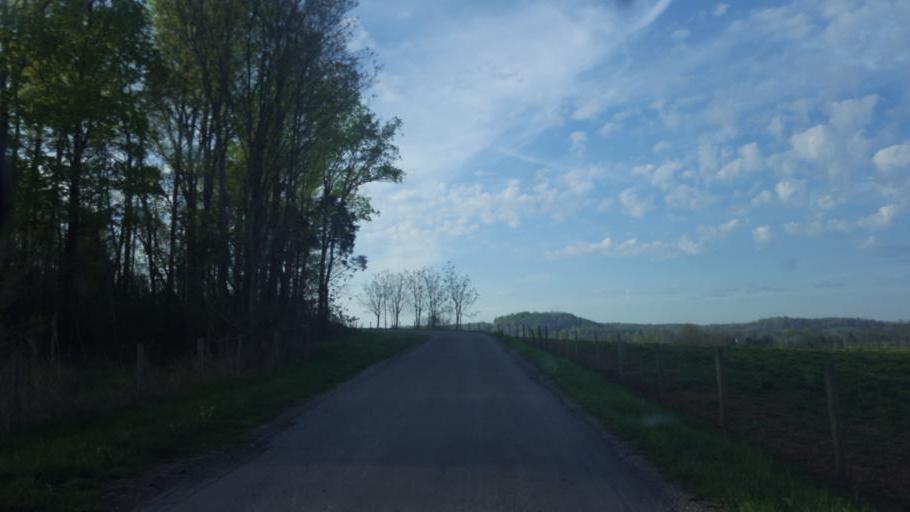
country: US
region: Kentucky
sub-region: Hart County
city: Munfordville
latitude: 37.2449
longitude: -85.9086
